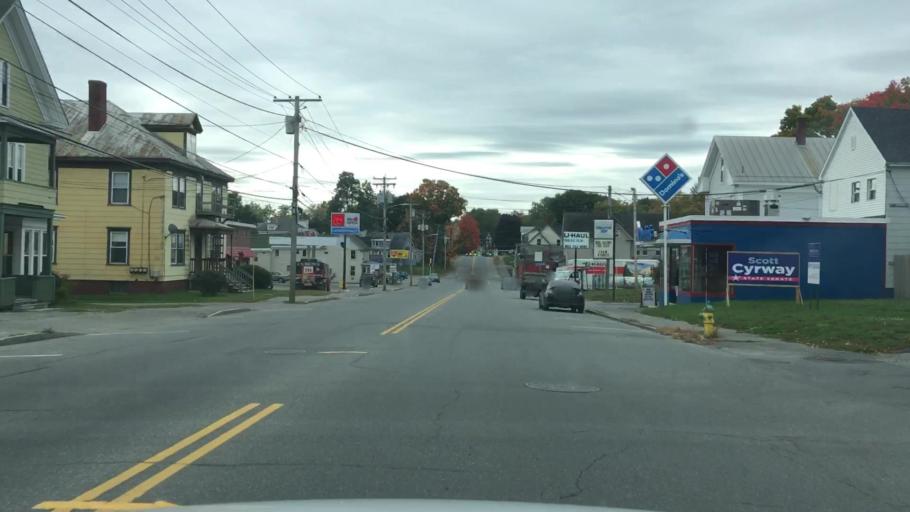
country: US
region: Maine
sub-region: Kennebec County
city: Waterville
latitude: 44.5489
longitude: -69.6341
